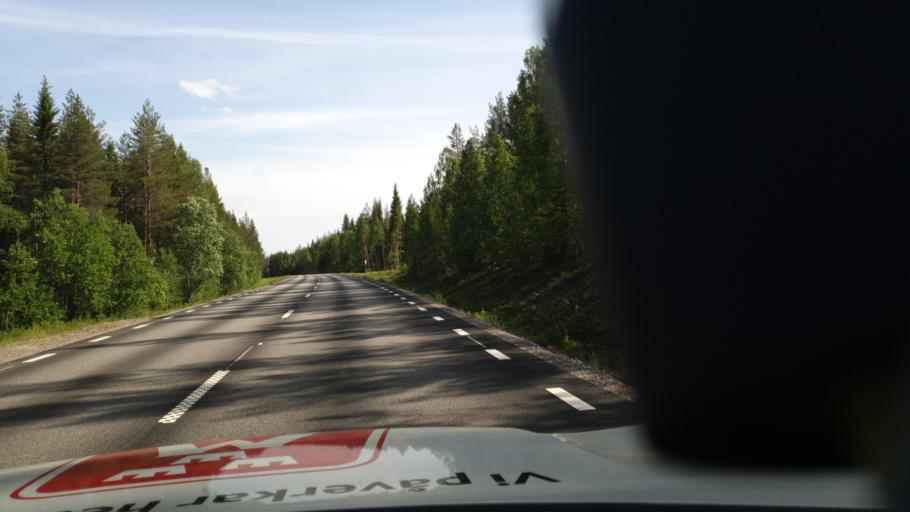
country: SE
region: Vaesterbotten
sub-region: Skelleftea Kommun
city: Boliden
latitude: 64.8918
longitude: 20.3760
